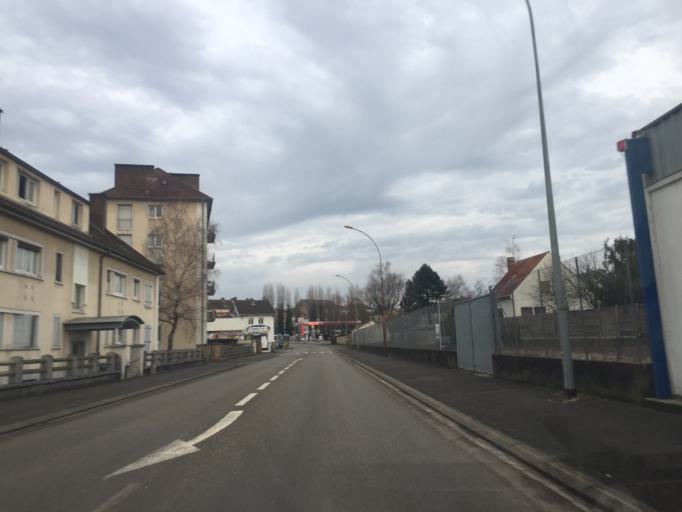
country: FR
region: Franche-Comte
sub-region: Departement du Jura
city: Dole
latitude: 47.0972
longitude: 5.5004
